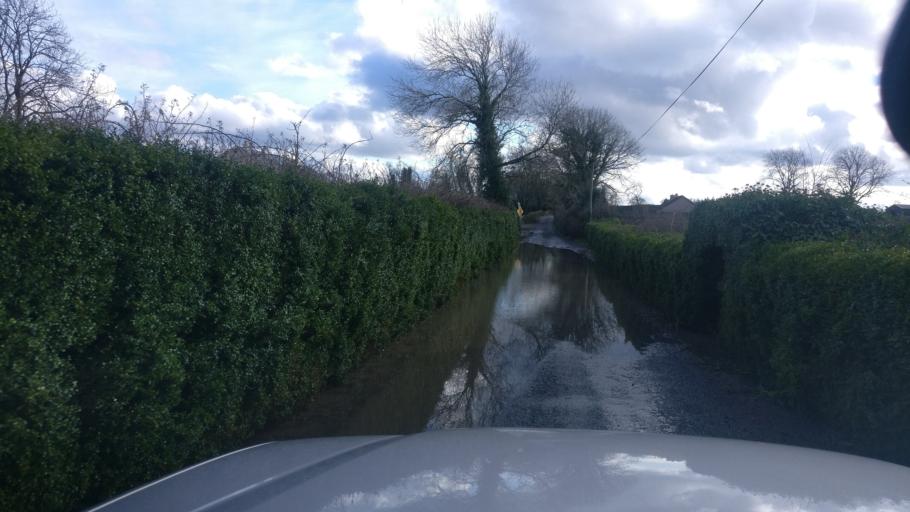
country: IE
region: Connaught
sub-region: County Galway
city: Loughrea
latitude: 53.1789
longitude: -8.4259
